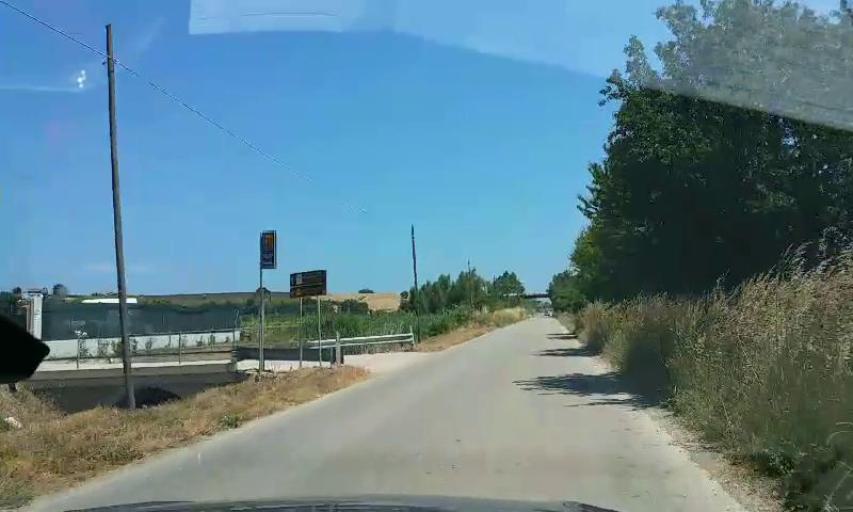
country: IT
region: Molise
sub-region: Provincia di Campobasso
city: San Giacomo degli Schiavoni
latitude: 41.9945
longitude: 14.9491
